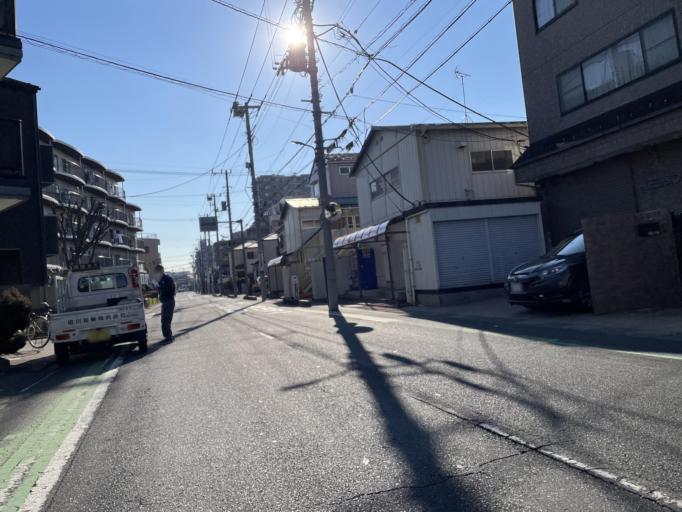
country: JP
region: Saitama
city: Soka
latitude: 35.8101
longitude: 139.7990
